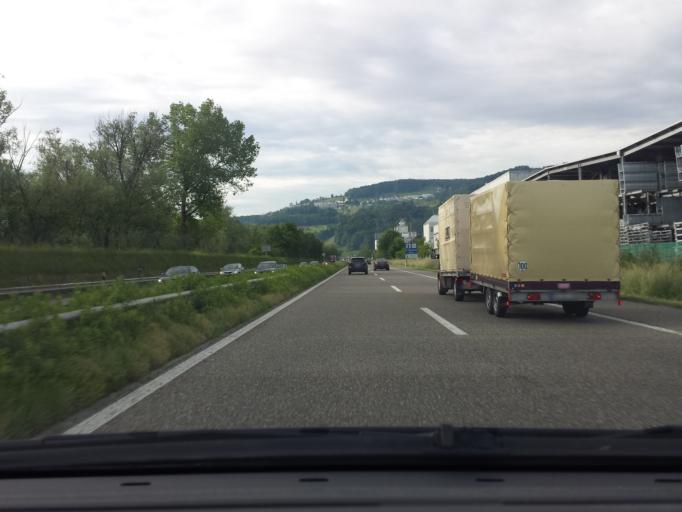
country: CH
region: Saint Gallen
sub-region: Wahlkreis Rheintal
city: Rheineck
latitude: 47.4757
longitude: 9.5861
